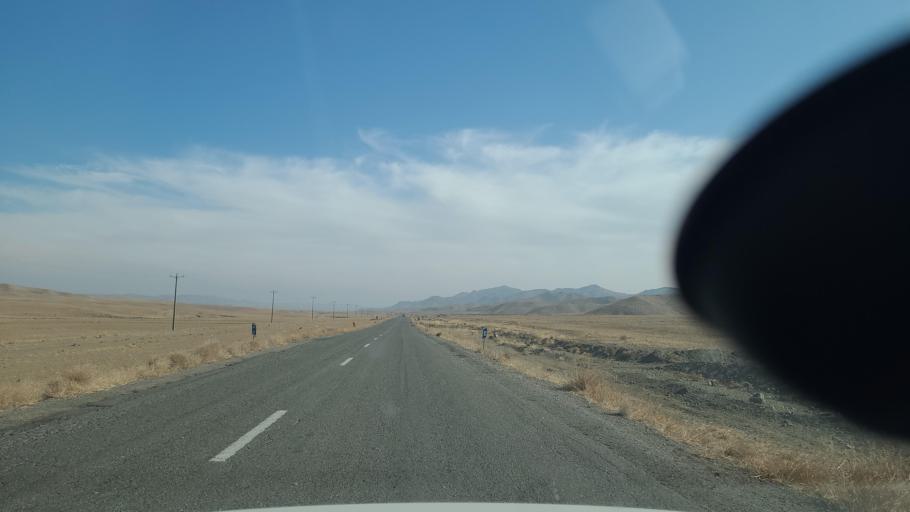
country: IR
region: Razavi Khorasan
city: Fariman
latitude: 35.5893
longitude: 59.6222
